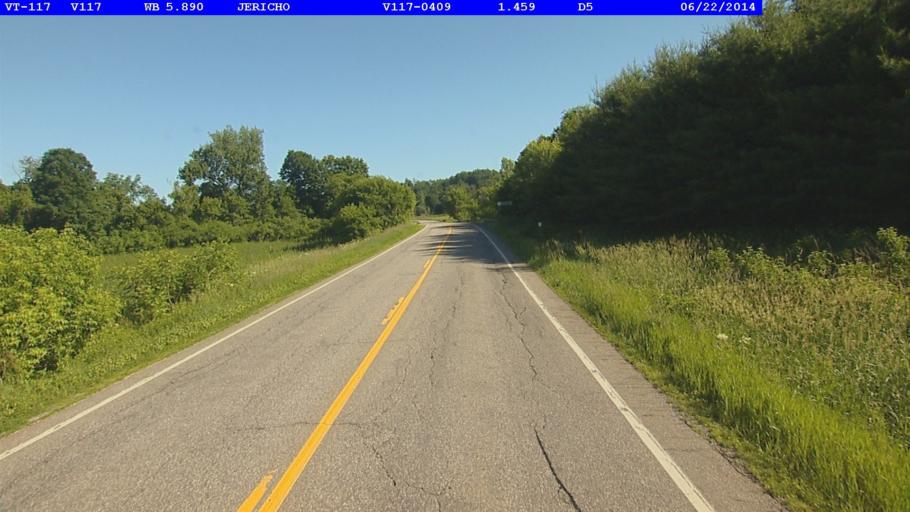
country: US
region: Vermont
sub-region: Chittenden County
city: Williston
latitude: 44.4540
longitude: -73.0179
